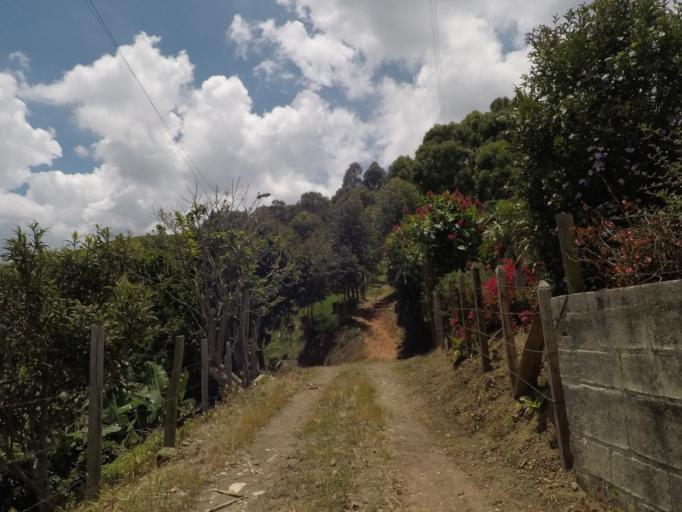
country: CO
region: Antioquia
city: Medellin
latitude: 6.2671
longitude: -75.6424
